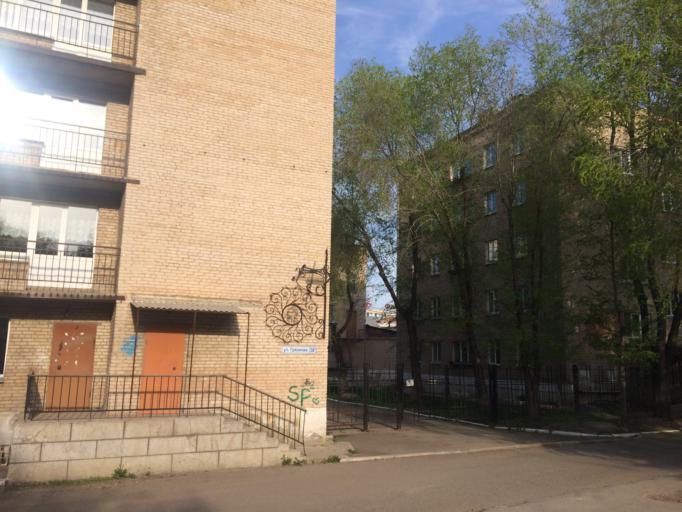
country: RU
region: Chelyabinsk
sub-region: Gorod Magnitogorsk
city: Magnitogorsk
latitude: 53.3967
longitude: 58.9832
